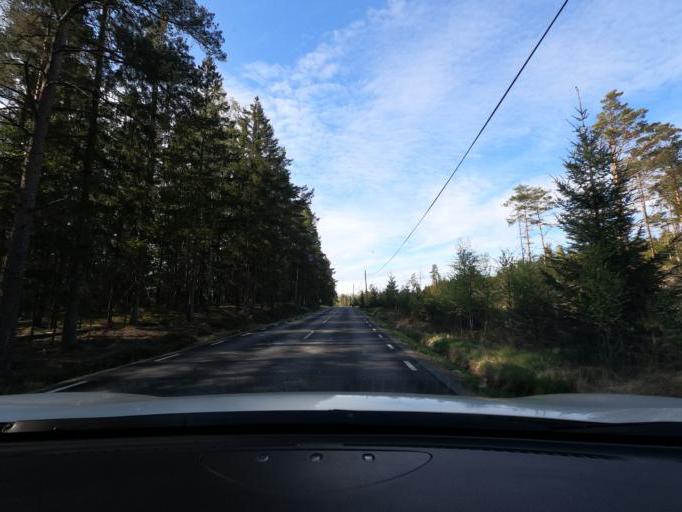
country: SE
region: Vaestra Goetaland
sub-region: Harryda Kommun
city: Landvetter
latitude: 57.6535
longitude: 12.2620
